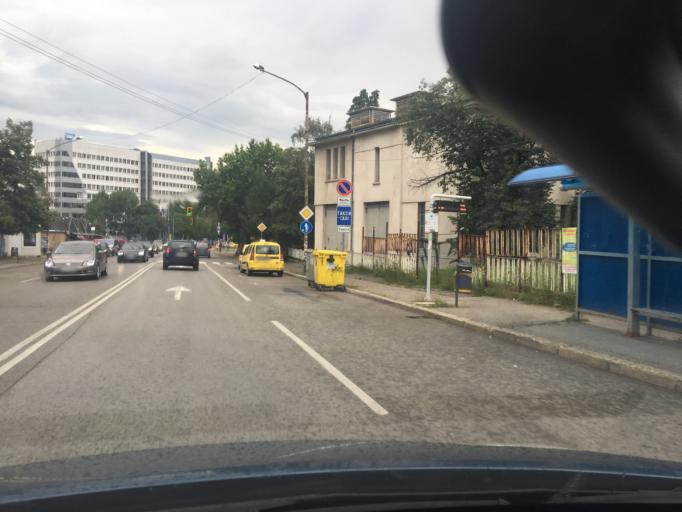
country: BG
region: Sofia-Capital
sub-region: Stolichna Obshtina
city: Sofia
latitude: 42.6669
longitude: 23.2662
